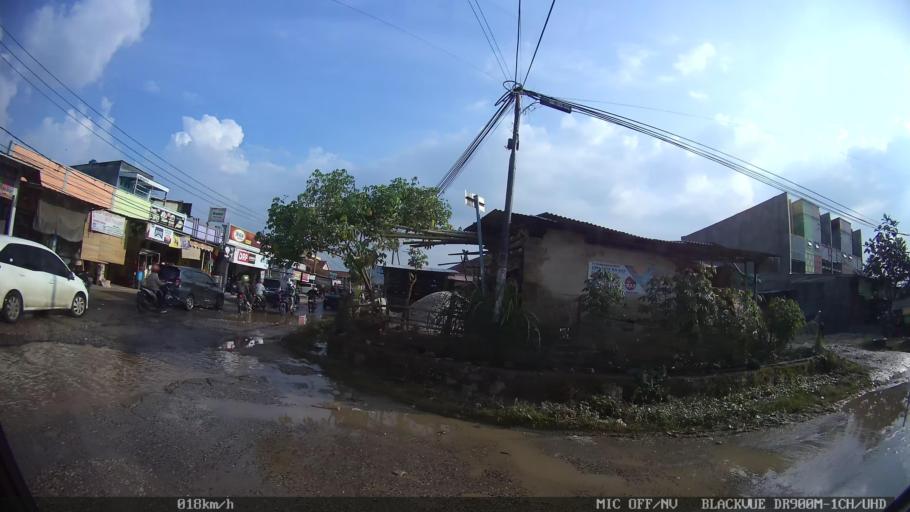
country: ID
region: Lampung
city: Kedaton
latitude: -5.3855
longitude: 105.3156
